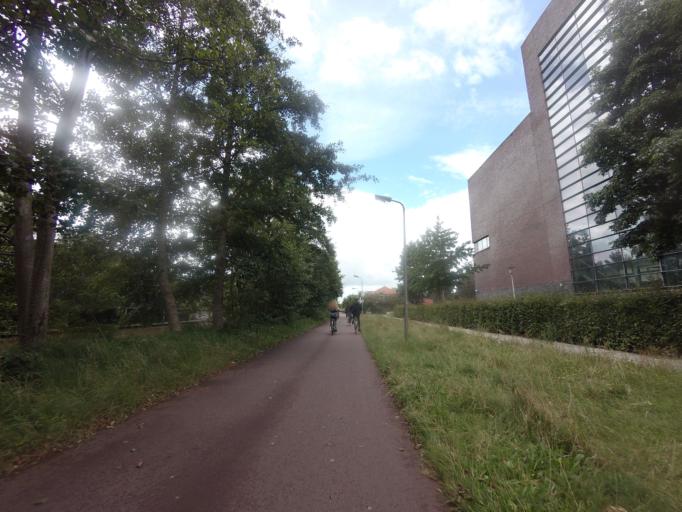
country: NL
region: Drenthe
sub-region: Gemeente Meppel
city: Meppel
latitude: 52.6944
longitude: 6.2014
